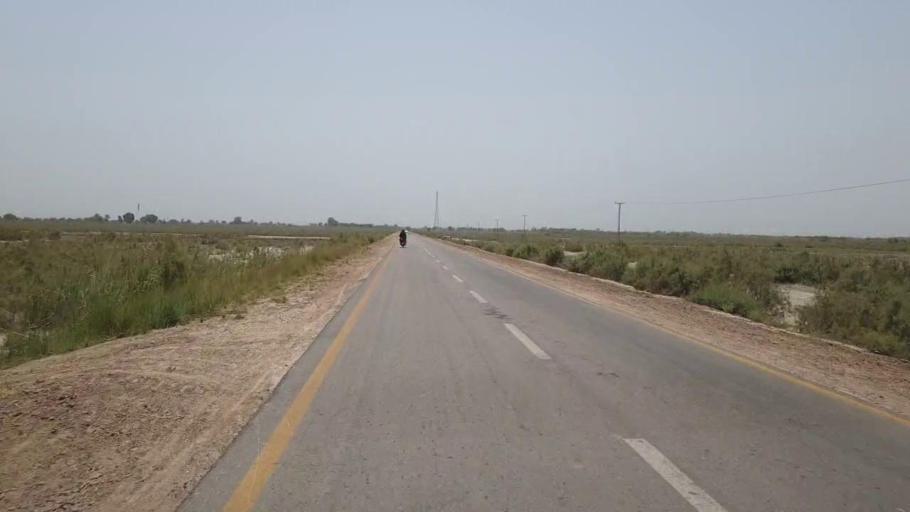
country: PK
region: Sindh
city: Moro
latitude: 26.6013
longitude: 68.0740
